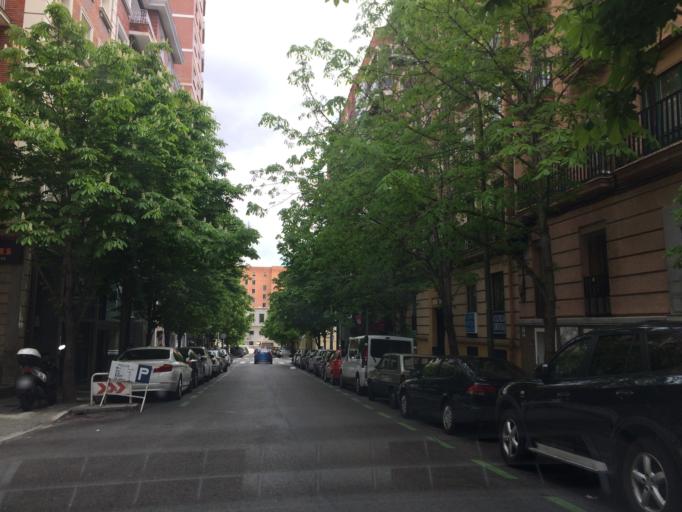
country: ES
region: Madrid
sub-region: Provincia de Madrid
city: Chamberi
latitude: 40.4429
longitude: -3.6968
